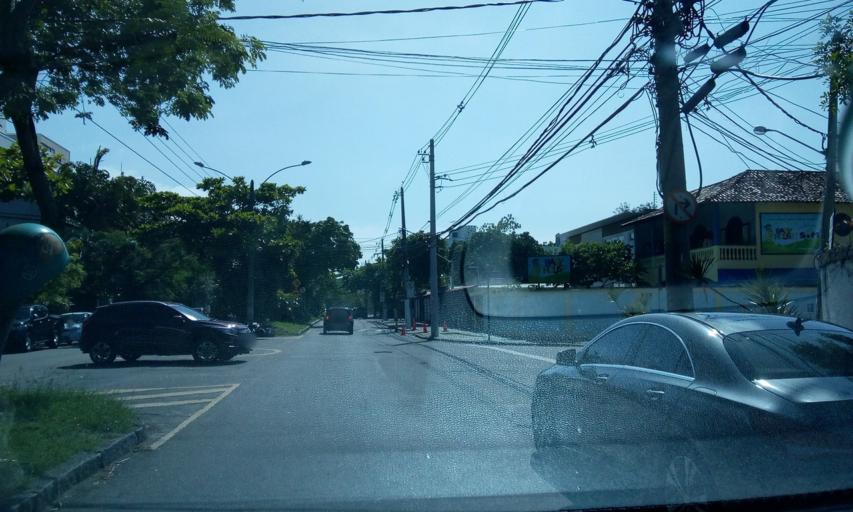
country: BR
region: Rio de Janeiro
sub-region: Nilopolis
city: Nilopolis
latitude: -23.0167
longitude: -43.4592
